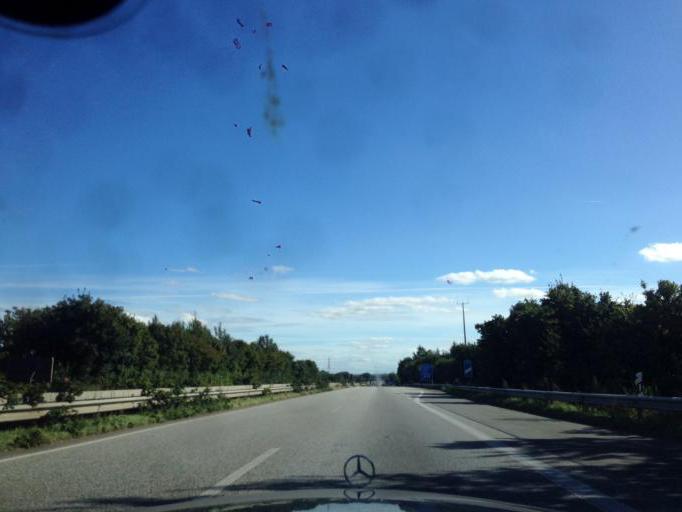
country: DE
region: Schleswig-Holstein
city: Jarplund-Weding
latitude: 54.7392
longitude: 9.3842
